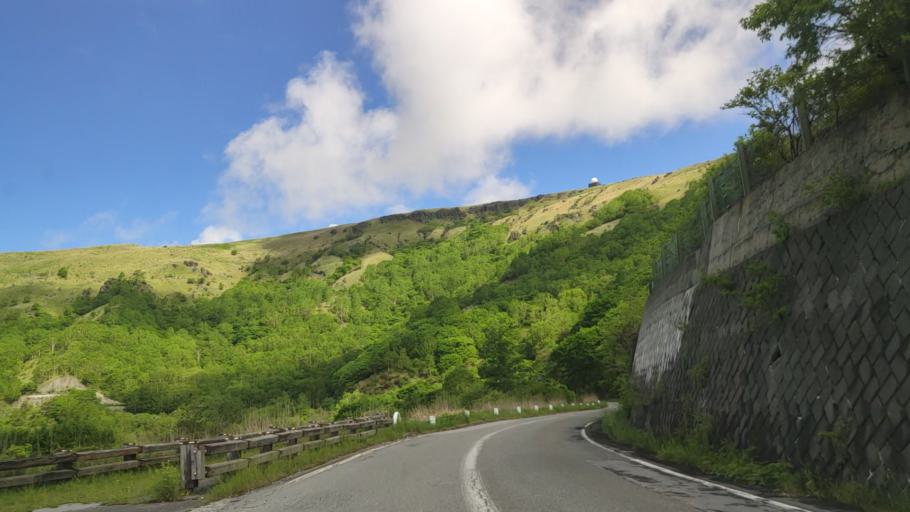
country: JP
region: Nagano
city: Suwa
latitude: 36.0963
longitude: 138.2010
